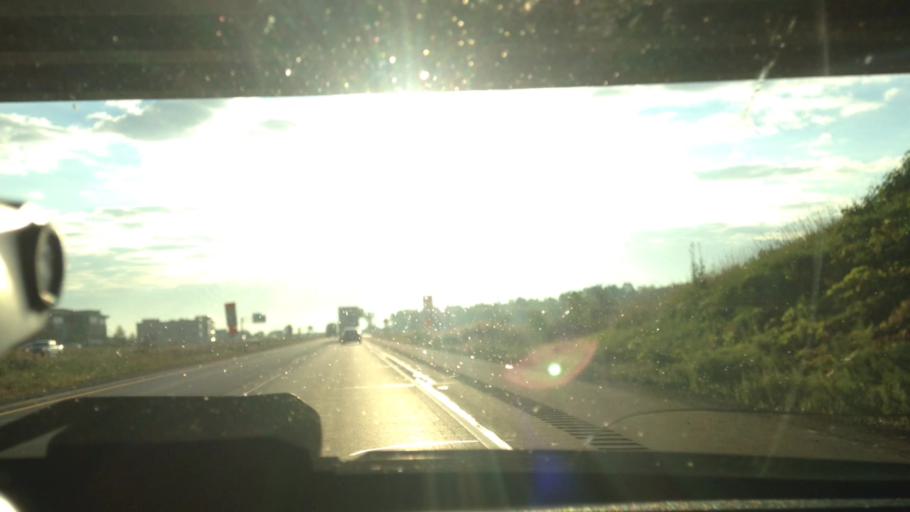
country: US
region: Wisconsin
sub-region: Outagamie County
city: Kimberly
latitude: 44.2980
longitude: -88.3751
